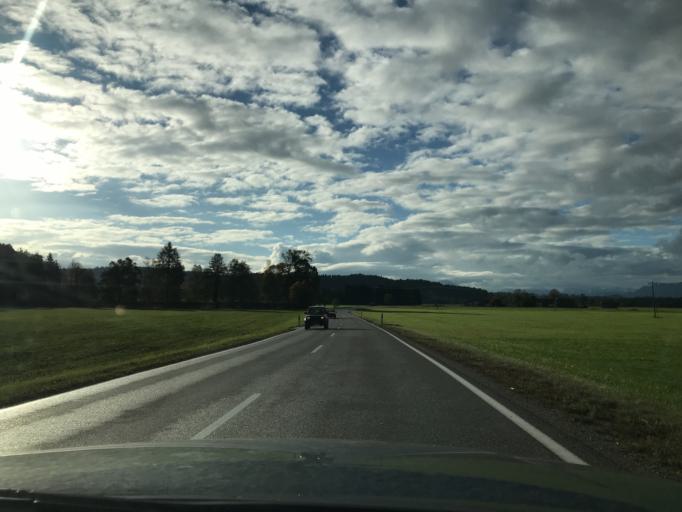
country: DE
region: Bavaria
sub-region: Upper Bavaria
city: Geretsried
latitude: 47.8404
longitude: 11.5276
